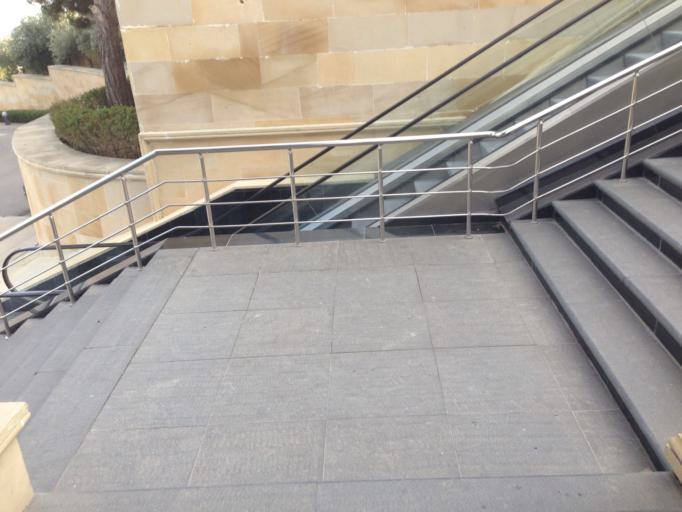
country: AZ
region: Baki
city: Badamdar
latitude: 40.3560
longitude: 49.8294
